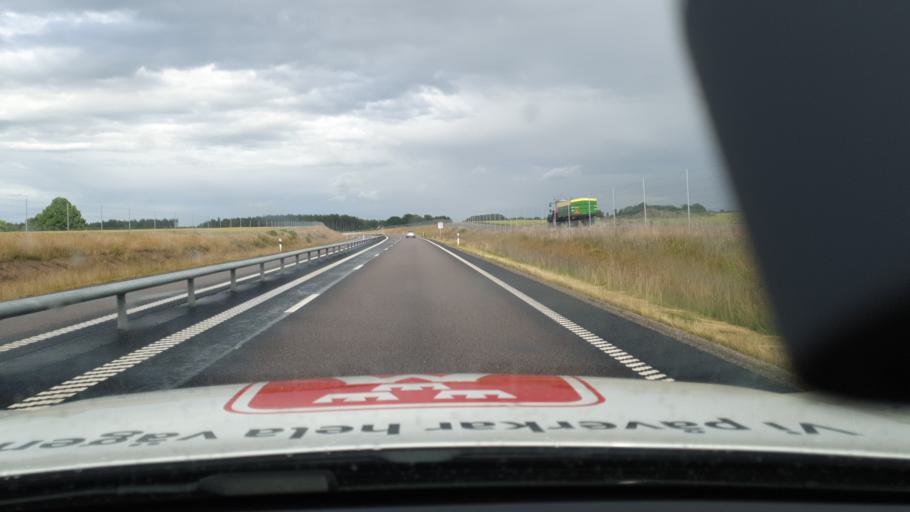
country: SE
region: Vaestra Goetaland
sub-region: Lidkopings Kommun
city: Vinninga
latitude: 58.4773
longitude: 13.2484
